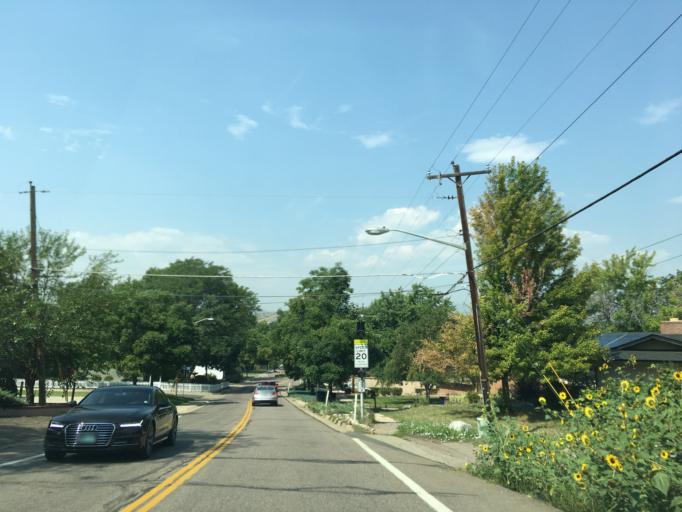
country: US
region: Colorado
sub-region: Jefferson County
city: Applewood
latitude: 39.7474
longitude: -105.1320
